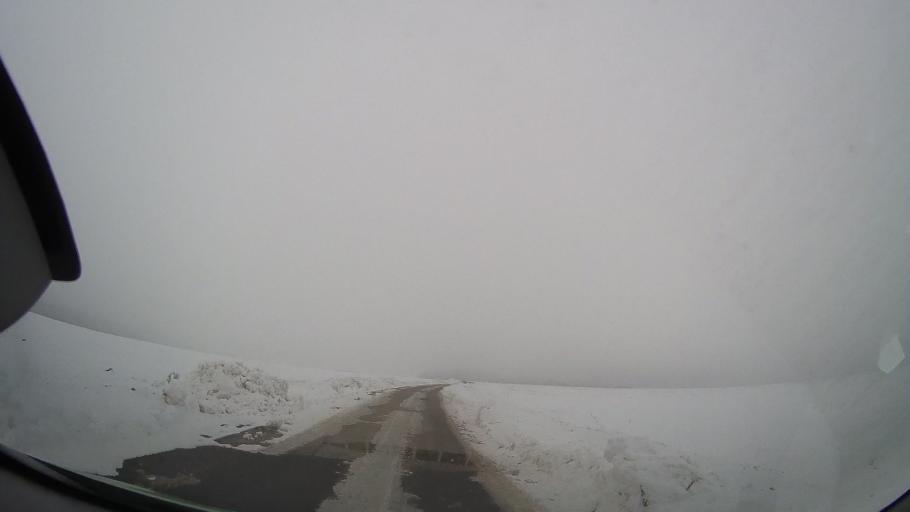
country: RO
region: Iasi
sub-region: Comuna Dagata
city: Dagata
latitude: 46.9051
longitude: 27.1927
